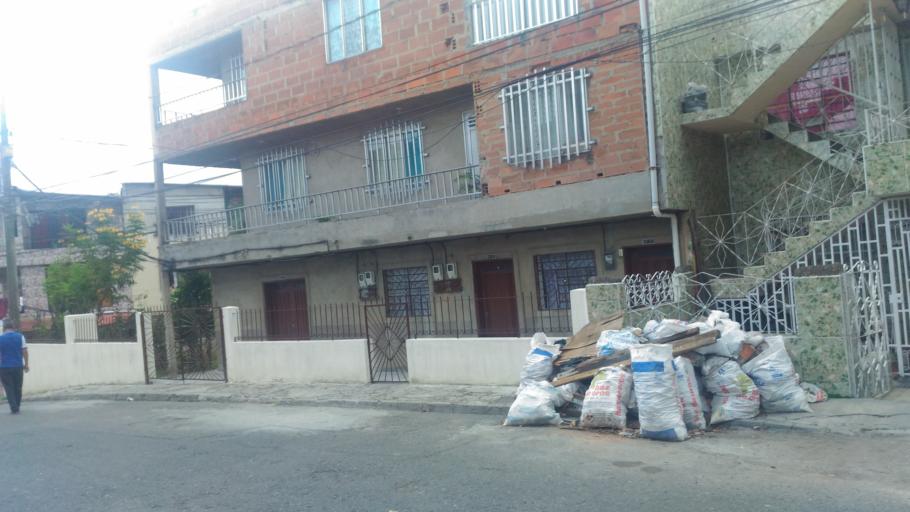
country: CO
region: Antioquia
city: Bello
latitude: 6.3010
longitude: -75.5739
